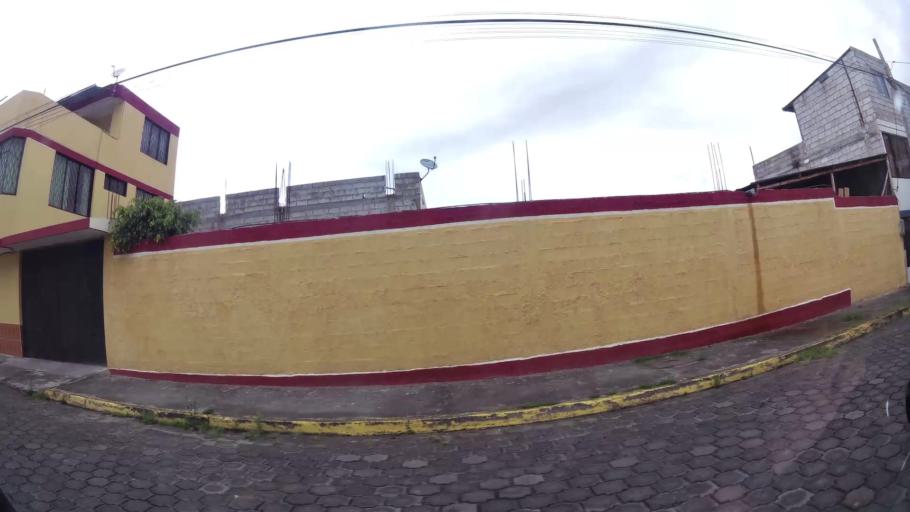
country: EC
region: Pichincha
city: Sangolqui
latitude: -0.3217
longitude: -78.4379
